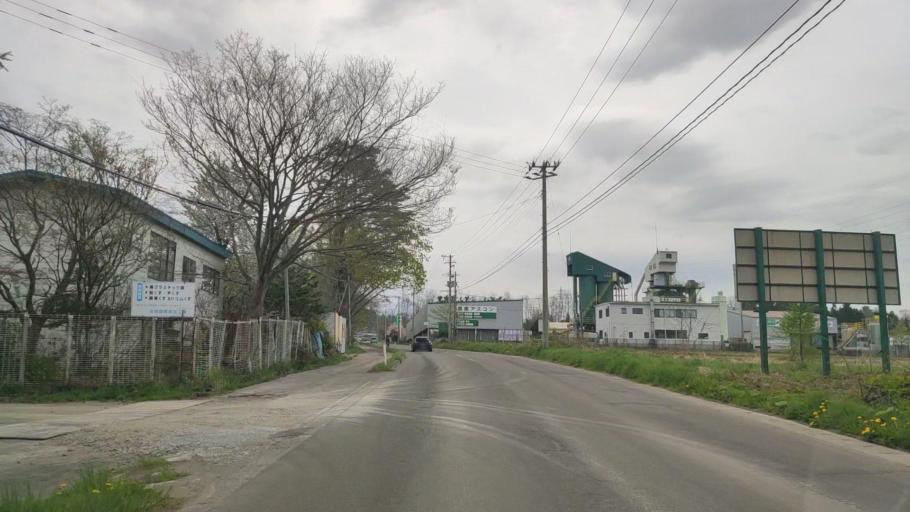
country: JP
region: Aomori
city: Aomori Shi
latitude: 40.7742
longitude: 140.7963
